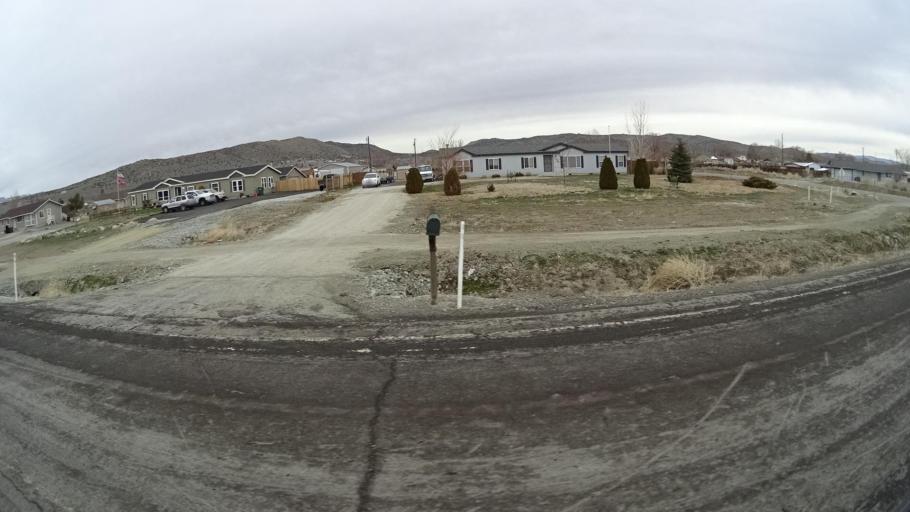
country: US
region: Nevada
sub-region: Washoe County
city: Lemmon Valley
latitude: 39.6740
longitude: -119.8433
